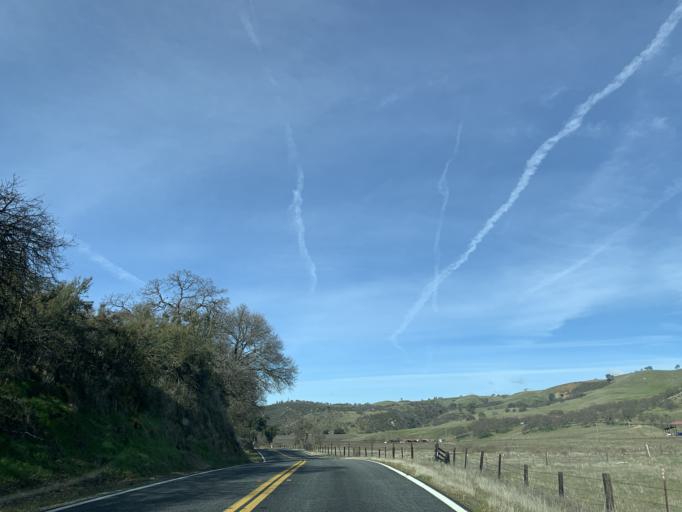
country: US
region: California
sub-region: Monterey County
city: Greenfield
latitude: 36.5091
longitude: -121.1130
